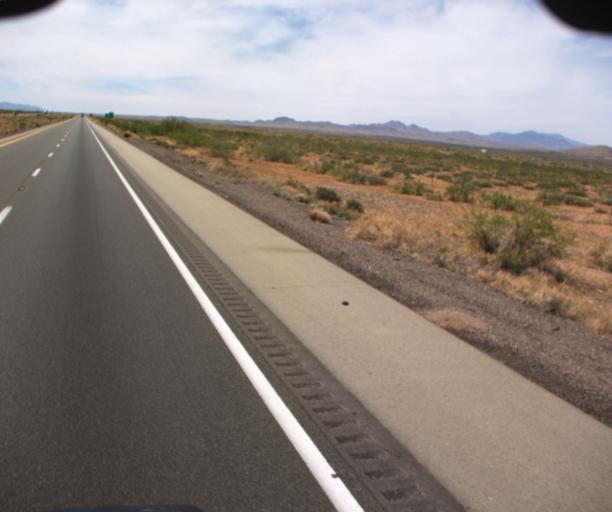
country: US
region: Arizona
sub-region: Cochise County
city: Willcox
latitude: 32.3442
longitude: -109.5824
